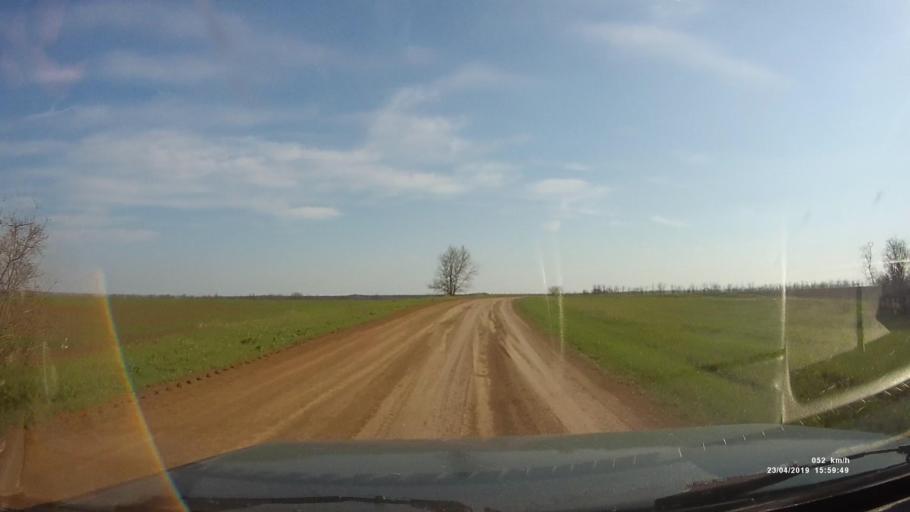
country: RU
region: Rostov
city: Remontnoye
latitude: 46.5139
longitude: 43.1094
